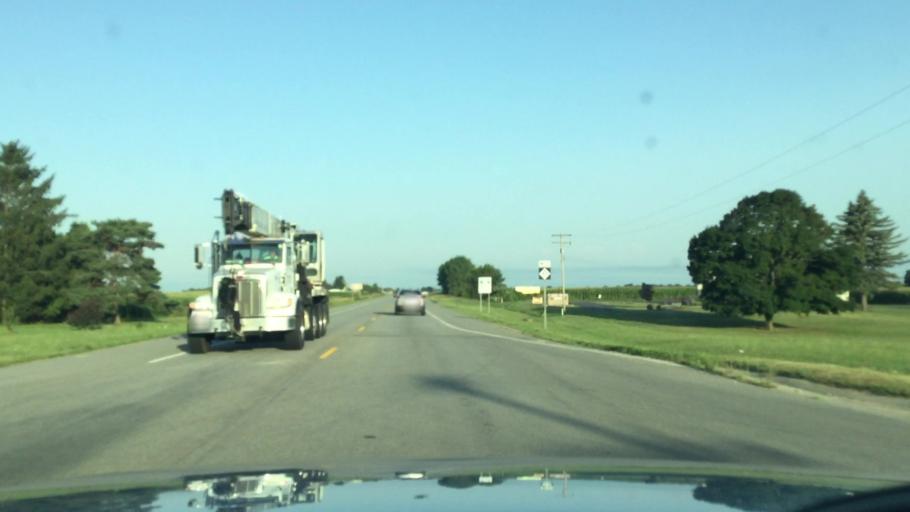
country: US
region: Michigan
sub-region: Gratiot County
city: Ithaca
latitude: 43.1761
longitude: -84.6794
